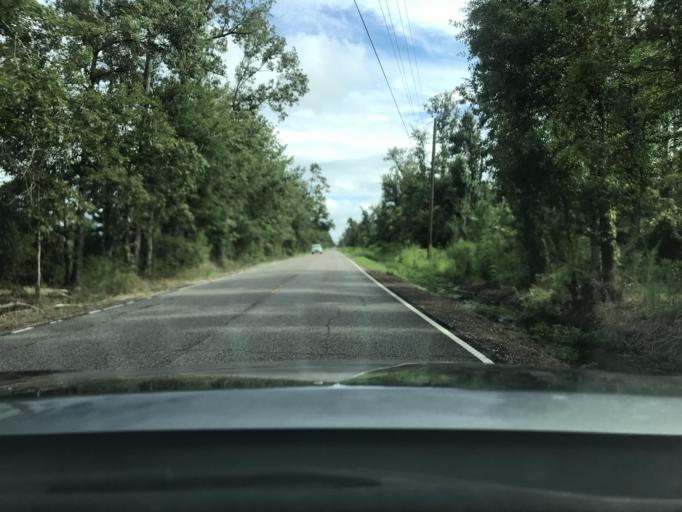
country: US
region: Louisiana
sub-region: Calcasieu Parish
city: Westlake
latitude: 30.2778
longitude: -93.2751
